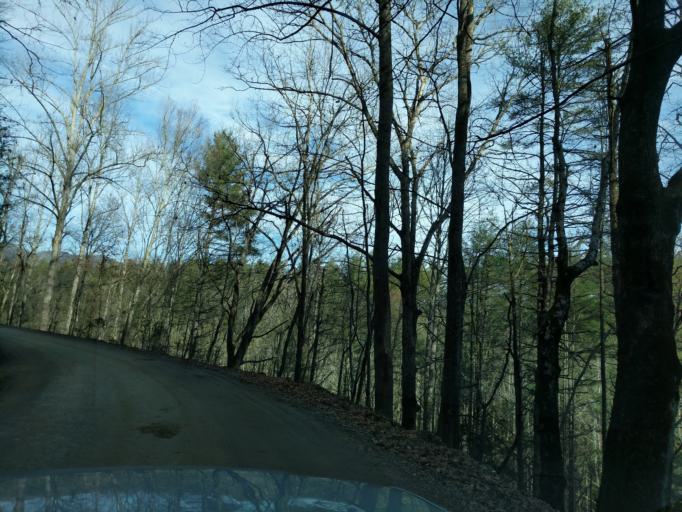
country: US
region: North Carolina
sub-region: Haywood County
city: Cove Creek
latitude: 35.6680
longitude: -83.0232
